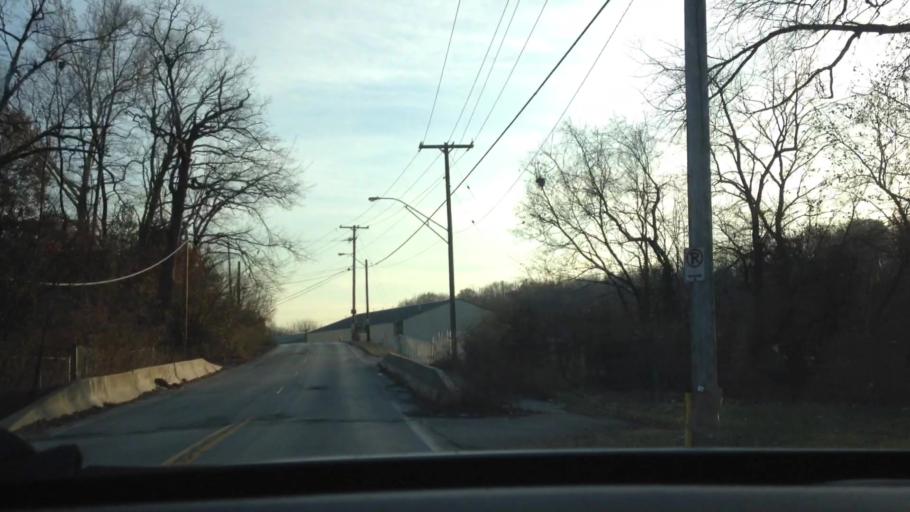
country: US
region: Missouri
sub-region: Clay County
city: North Kansas City
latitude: 39.1565
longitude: -94.5473
